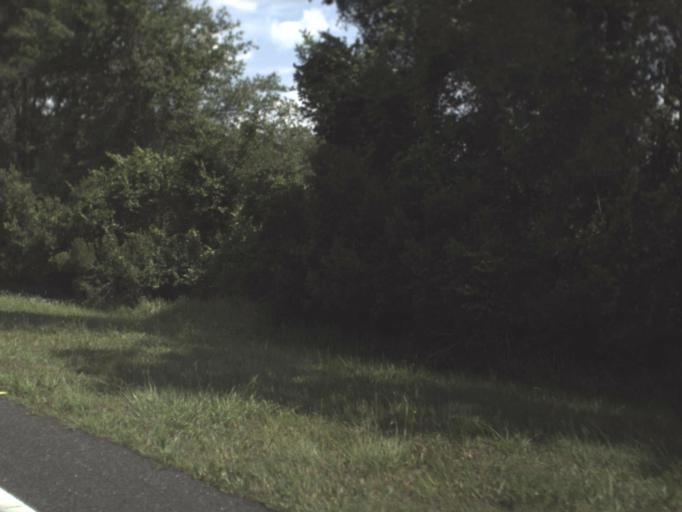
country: US
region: Florida
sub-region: Alachua County
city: Waldo
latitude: 29.7671
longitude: -82.1488
